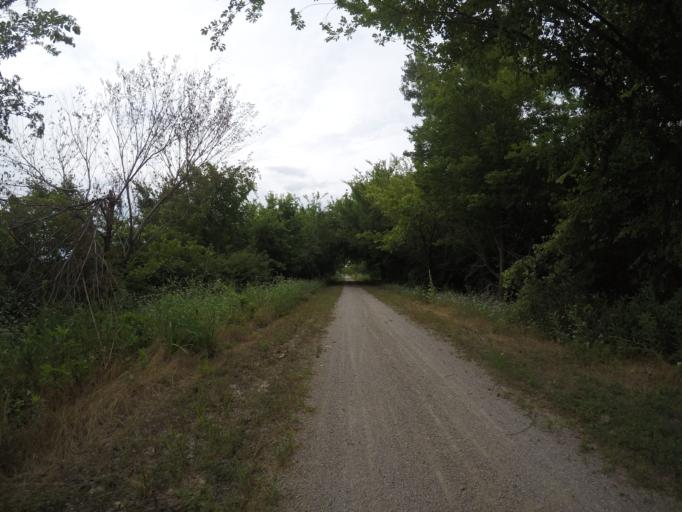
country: US
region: Kansas
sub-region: Franklin County
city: Ottawa
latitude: 38.5201
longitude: -95.2724
